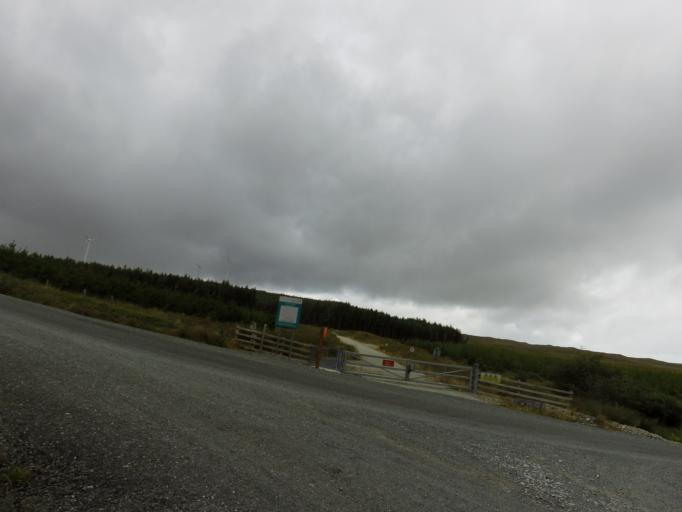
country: IE
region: Connaught
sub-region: County Galway
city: Oughterard
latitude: 53.3829
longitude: -9.3745
